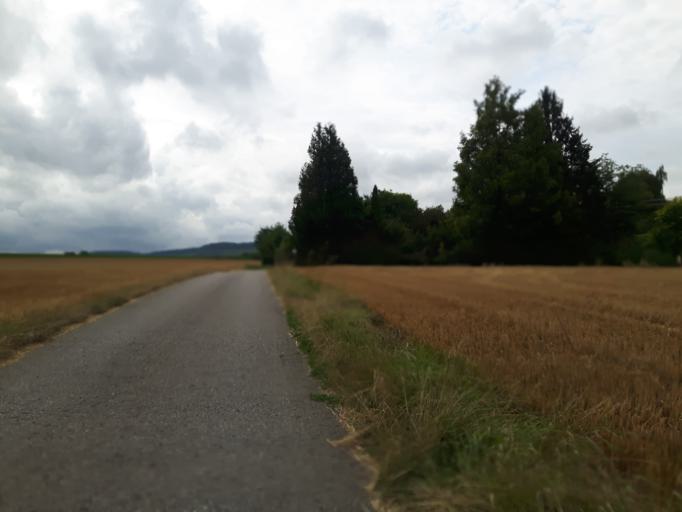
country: DE
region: Baden-Wuerttemberg
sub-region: Regierungsbezirk Stuttgart
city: Nordheim
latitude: 49.1109
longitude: 9.1163
